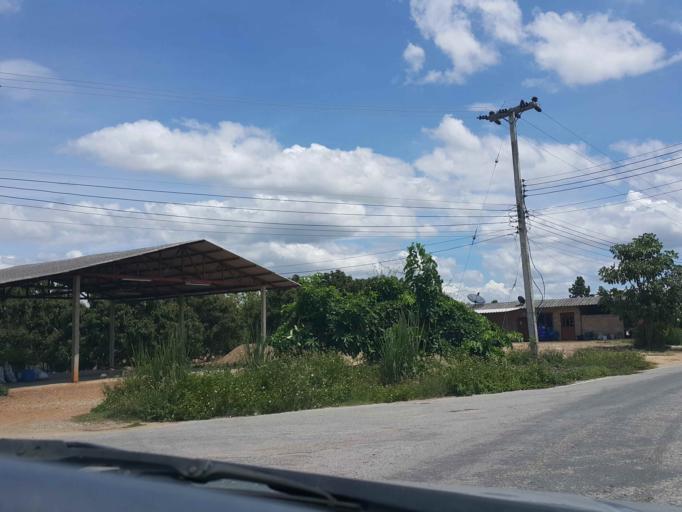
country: TH
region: Chiang Mai
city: Doi Lo
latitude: 18.5244
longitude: 98.7759
